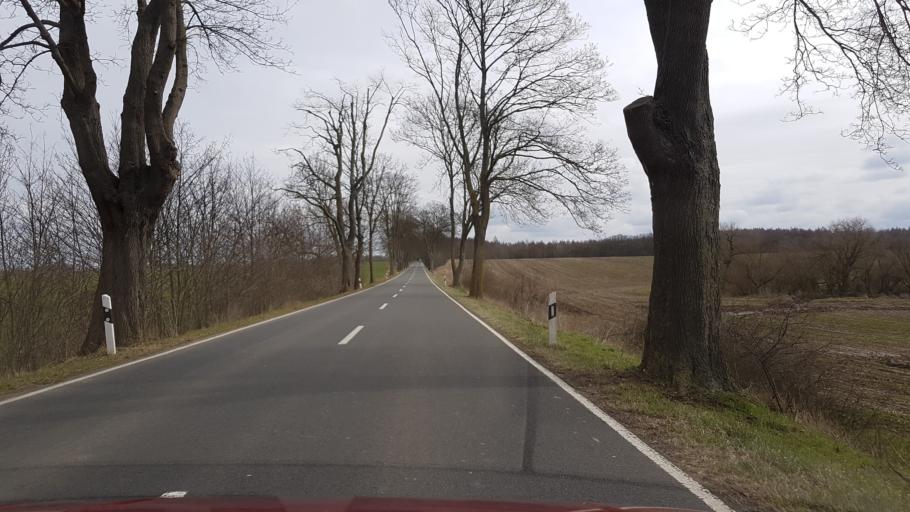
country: DE
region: Brandenburg
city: Mescherin
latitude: 53.2655
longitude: 14.4107
